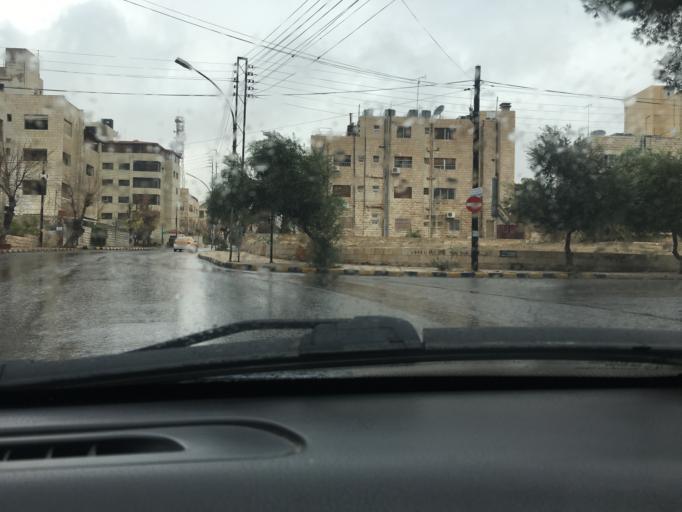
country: JO
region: Amman
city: Amman
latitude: 31.9679
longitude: 35.9105
